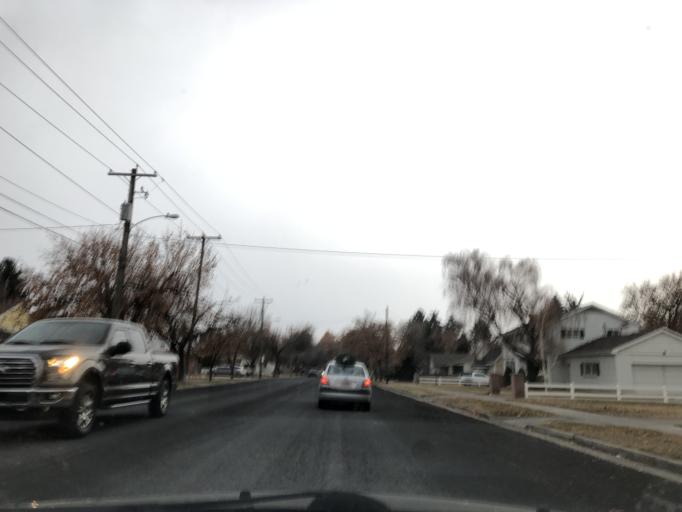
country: US
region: Utah
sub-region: Cache County
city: Logan
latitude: 41.7445
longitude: -111.8295
